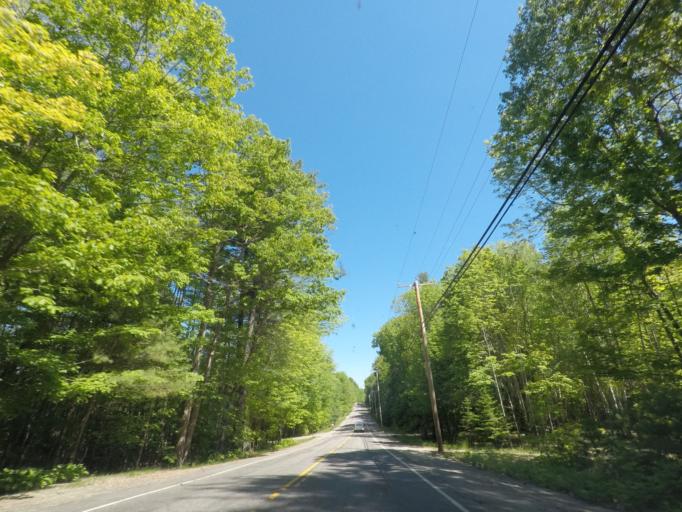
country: US
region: Maine
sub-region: Kennebec County
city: Manchester
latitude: 44.2875
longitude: -69.8892
